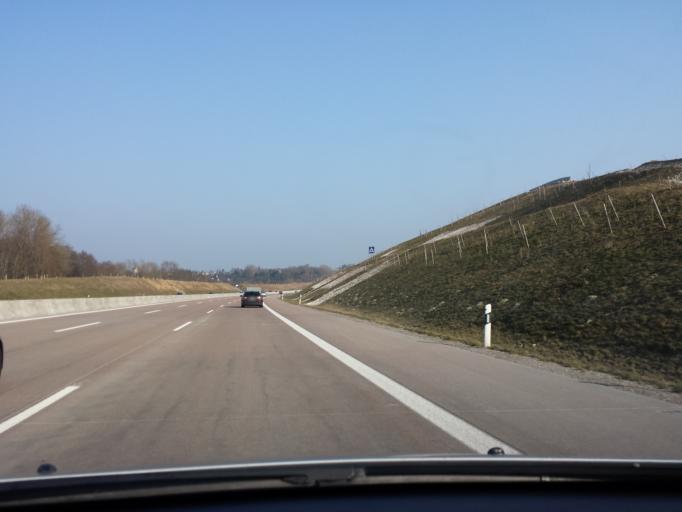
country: DE
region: Bavaria
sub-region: Swabia
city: Rettenbach
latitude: 48.4316
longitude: 10.3637
